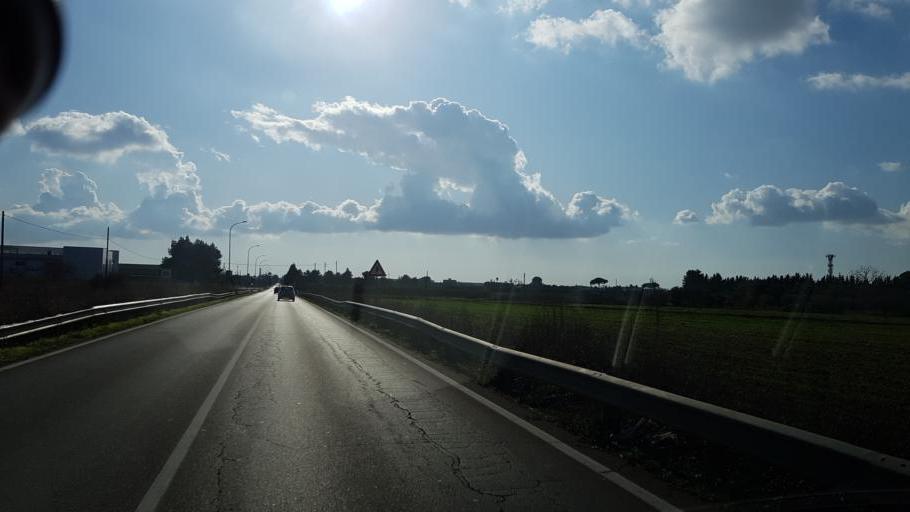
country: IT
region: Apulia
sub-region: Provincia di Lecce
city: Salice Salentino
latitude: 40.3980
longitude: 17.9705
